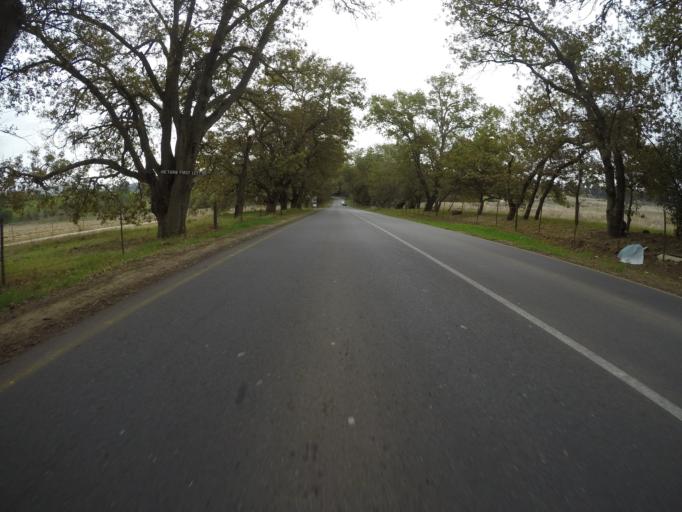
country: ZA
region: Western Cape
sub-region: City of Cape Town
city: Kraaifontein
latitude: -33.8480
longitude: 18.6283
